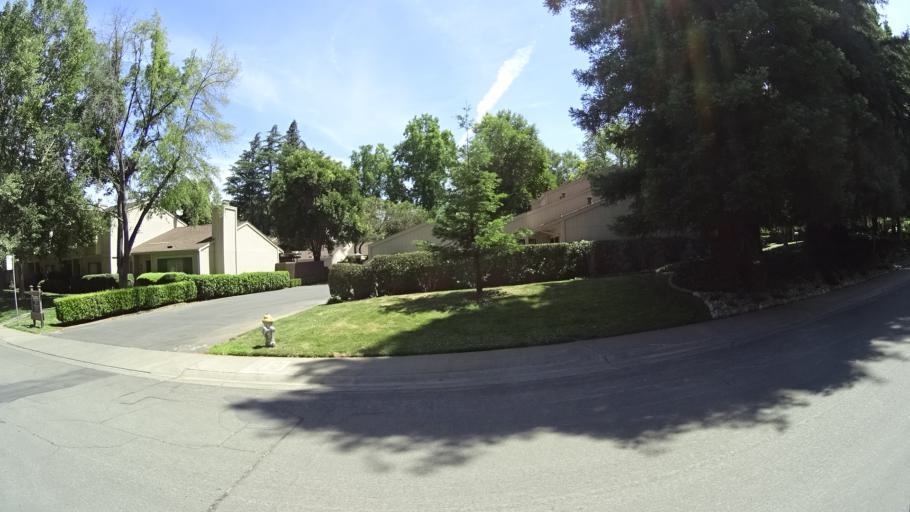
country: US
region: California
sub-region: Sacramento County
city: Arden-Arcade
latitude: 38.5649
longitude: -121.4176
